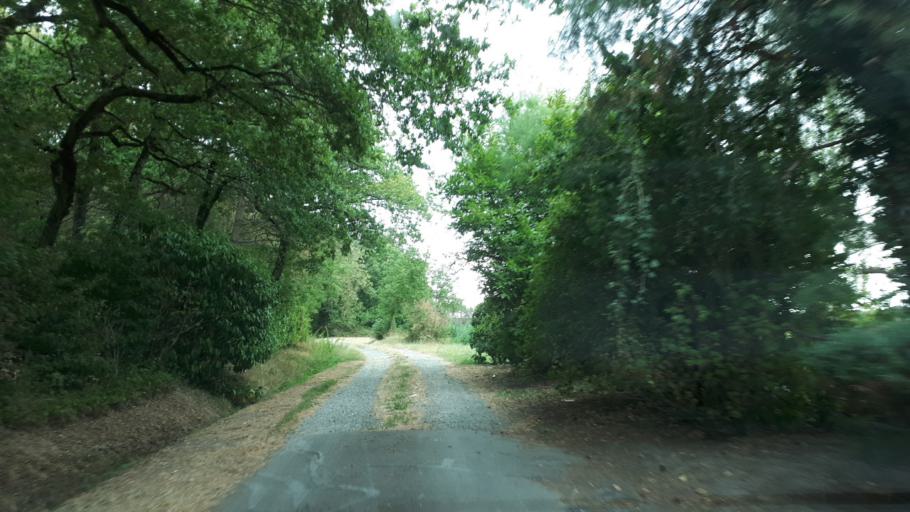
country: FR
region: Centre
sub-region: Departement du Loir-et-Cher
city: Saint-Romain-sur-Cher
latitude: 47.3545
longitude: 1.3934
